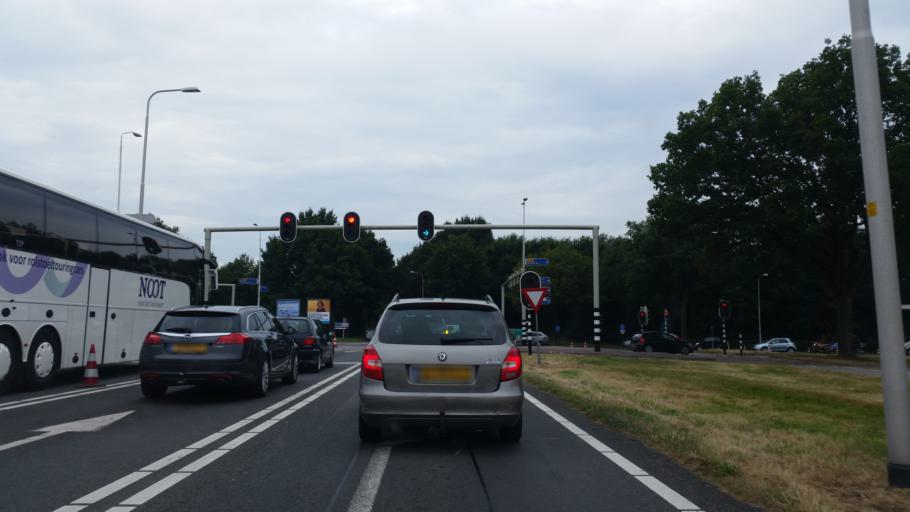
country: NL
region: Gelderland
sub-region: Gemeente Ede
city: Ede
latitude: 52.0515
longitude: 5.6762
